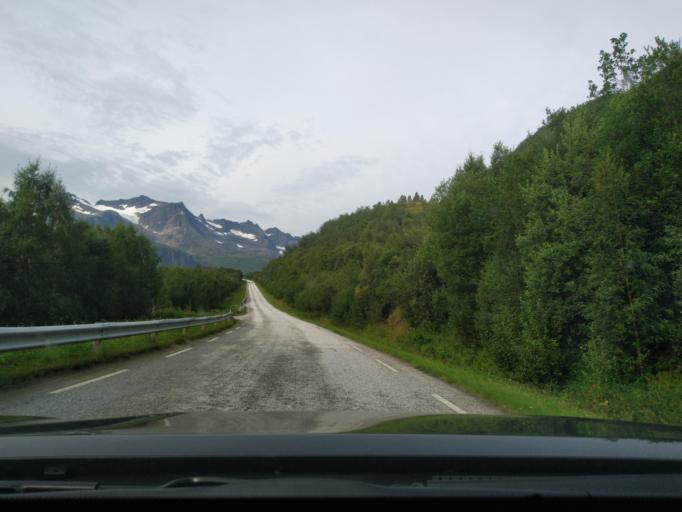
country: NO
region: Troms
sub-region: Dyroy
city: Brostadbotn
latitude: 68.9097
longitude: 17.5143
